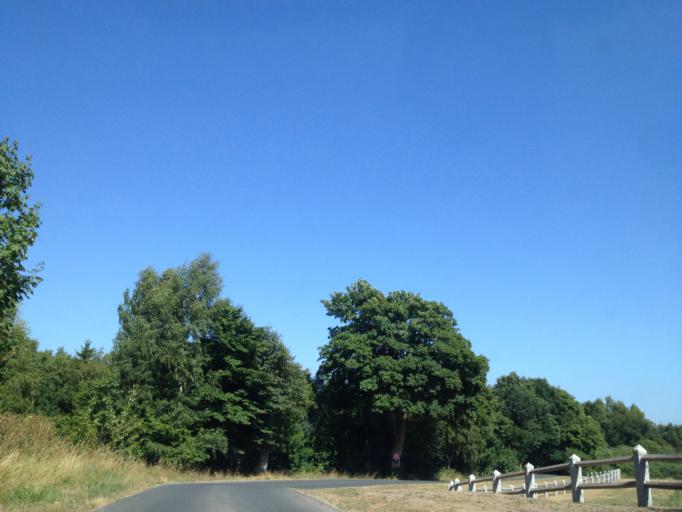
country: DK
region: Capital Region
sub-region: Helsingor Kommune
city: Hornbaek
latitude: 56.0140
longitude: 12.4708
